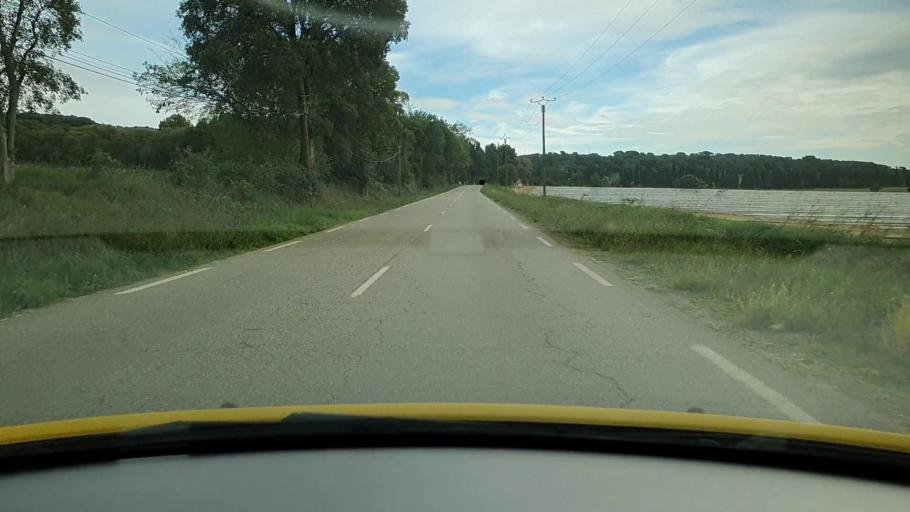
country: FR
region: Languedoc-Roussillon
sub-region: Departement du Gard
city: Garons
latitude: 43.7355
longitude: 4.4673
